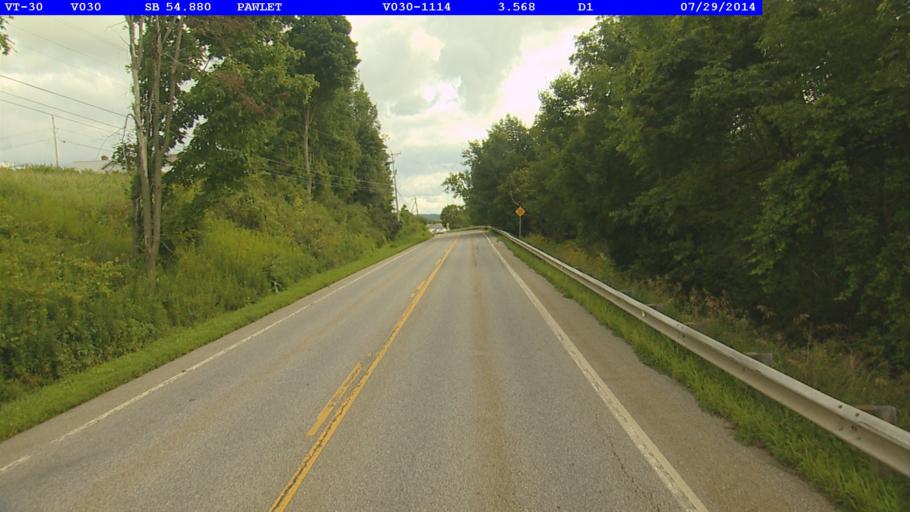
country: US
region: New York
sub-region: Washington County
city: Granville
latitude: 43.3586
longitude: -73.1846
